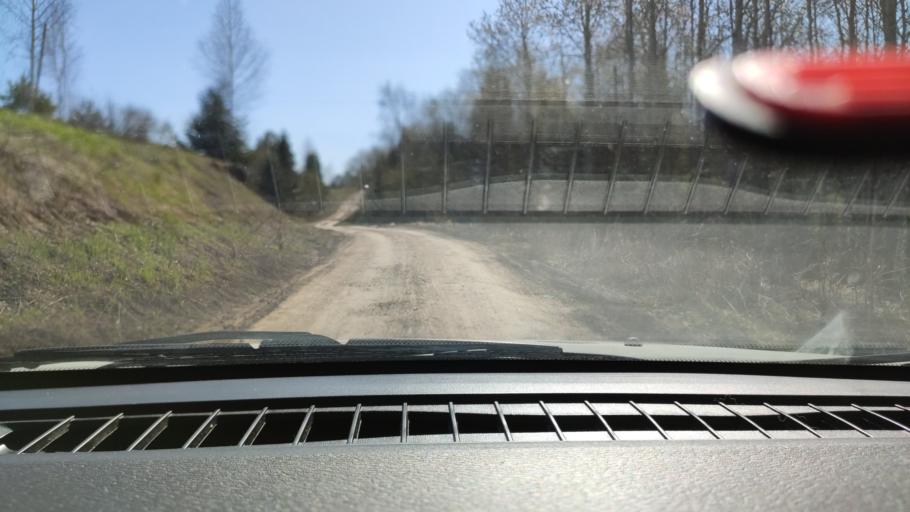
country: RU
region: Perm
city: Bershet'
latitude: 57.7239
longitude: 56.3947
